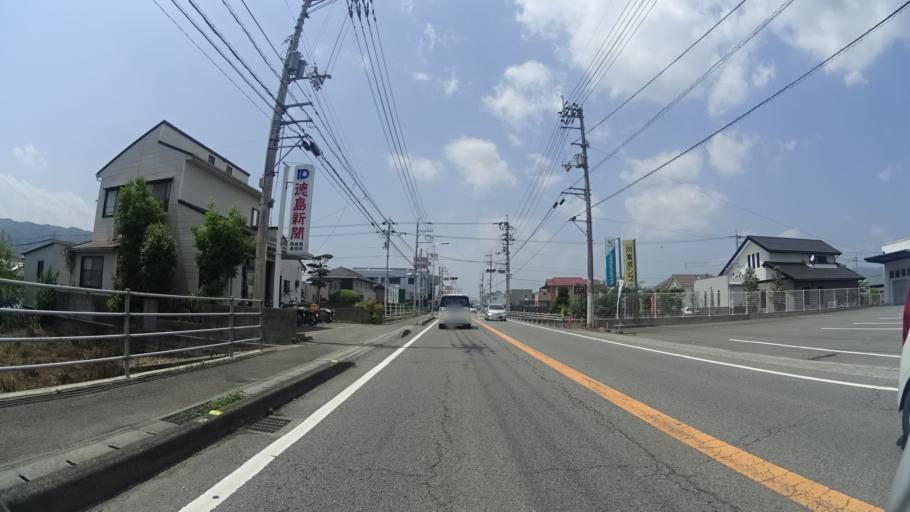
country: JP
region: Tokushima
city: Kamojimacho-jogejima
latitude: 34.0685
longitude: 134.3456
